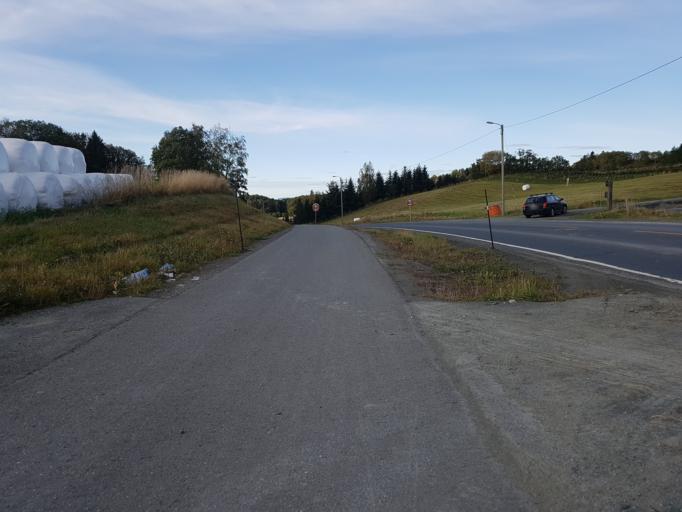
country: NO
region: Sor-Trondelag
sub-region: Trondheim
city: Trondheim
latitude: 63.3679
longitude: 10.4420
